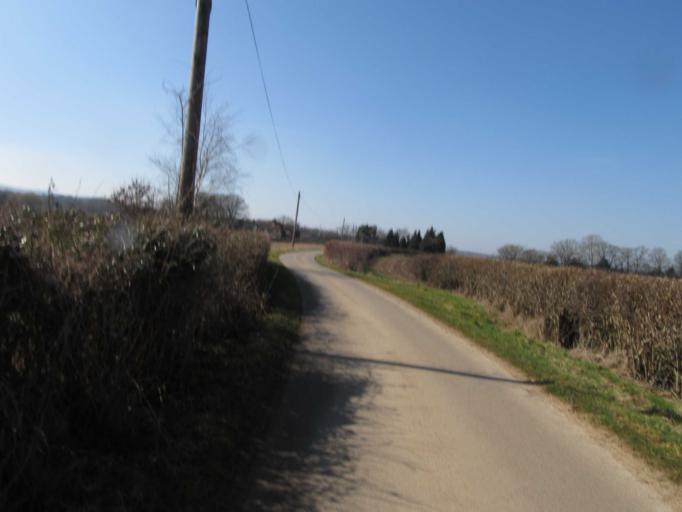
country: GB
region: England
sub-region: West Sussex
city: Petworth
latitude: 50.9684
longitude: -0.6135
